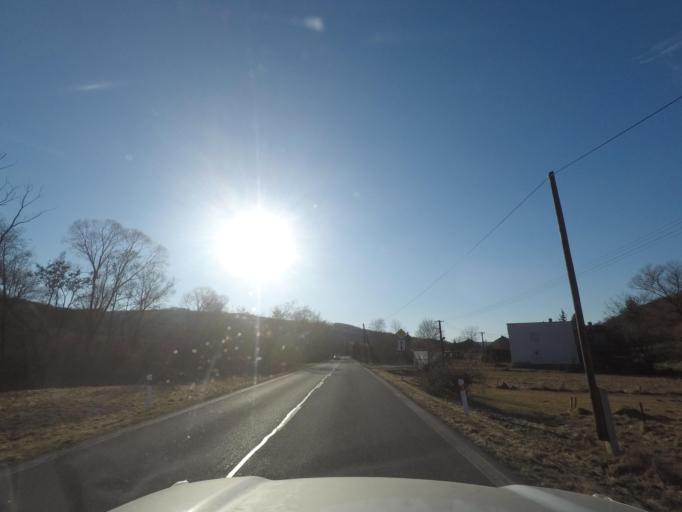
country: SK
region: Presovsky
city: Stropkov
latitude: 49.2567
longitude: 21.7598
